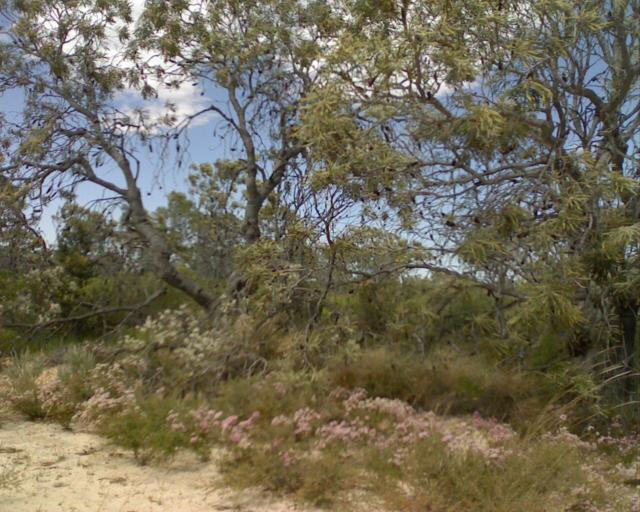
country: AU
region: Western Australia
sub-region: Moora
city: Moora
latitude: -30.0437
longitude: 115.6904
